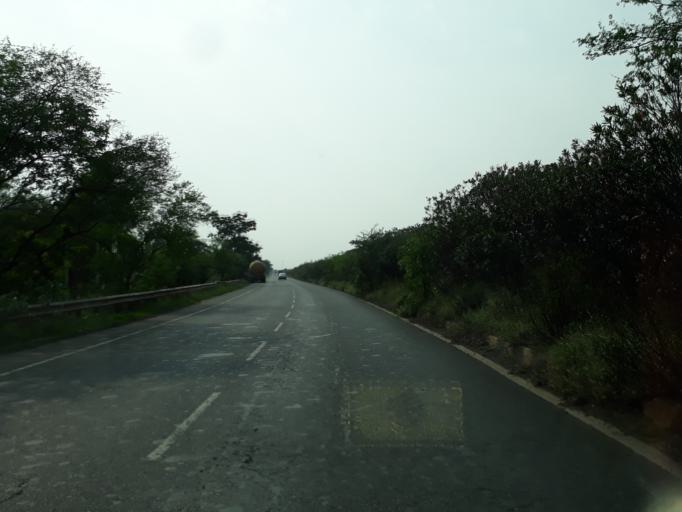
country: IN
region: West Bengal
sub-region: Purba Medinipur
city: Mahishadal
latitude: 22.1727
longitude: 87.9394
